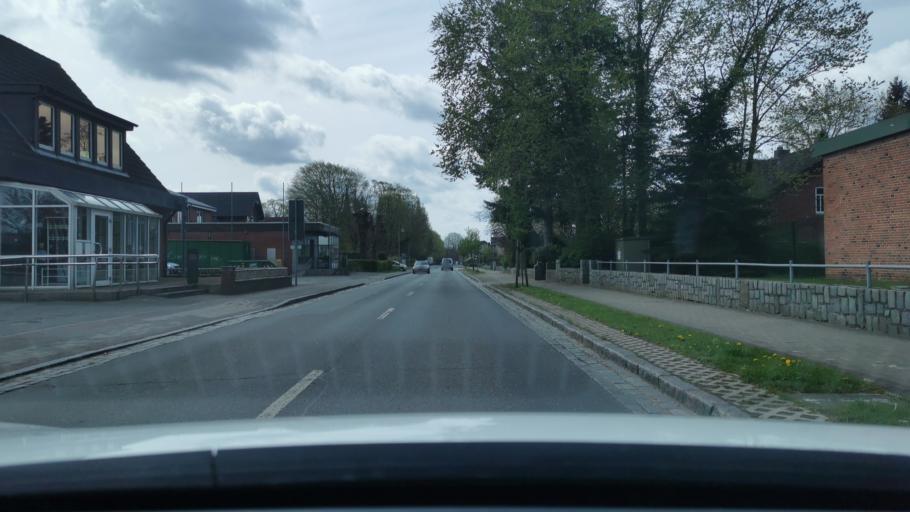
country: DE
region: Schleswig-Holstein
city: Hamdorf
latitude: 54.2246
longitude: 9.5190
